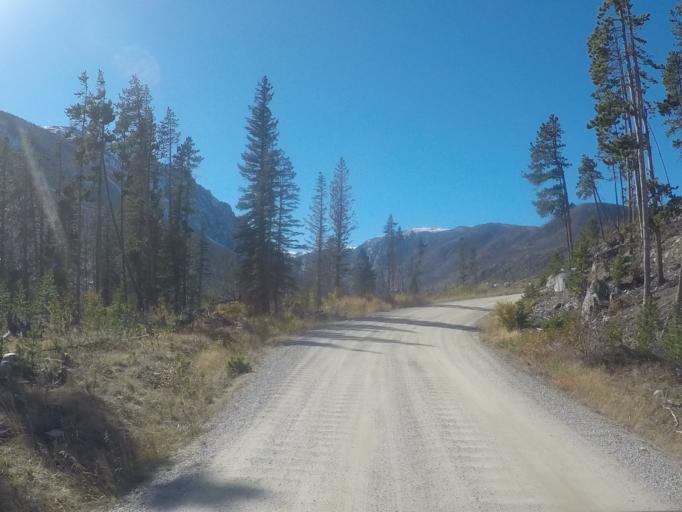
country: US
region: Montana
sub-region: Carbon County
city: Red Lodge
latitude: 45.1732
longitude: -109.4573
